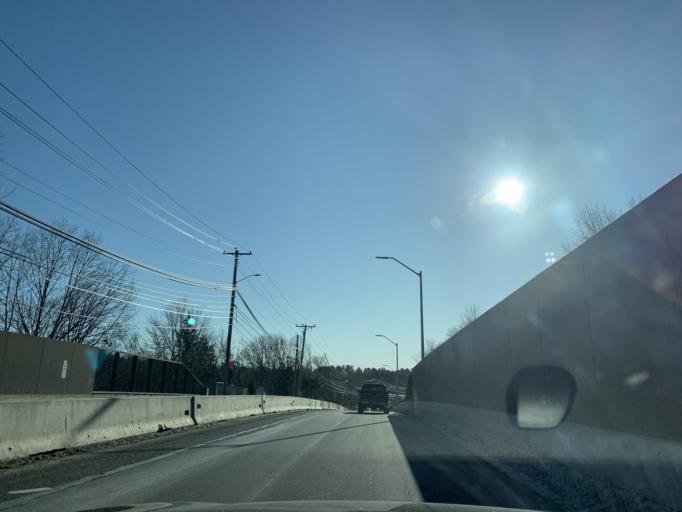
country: US
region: Massachusetts
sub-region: Norfolk County
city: Canton
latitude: 42.1963
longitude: -71.1542
